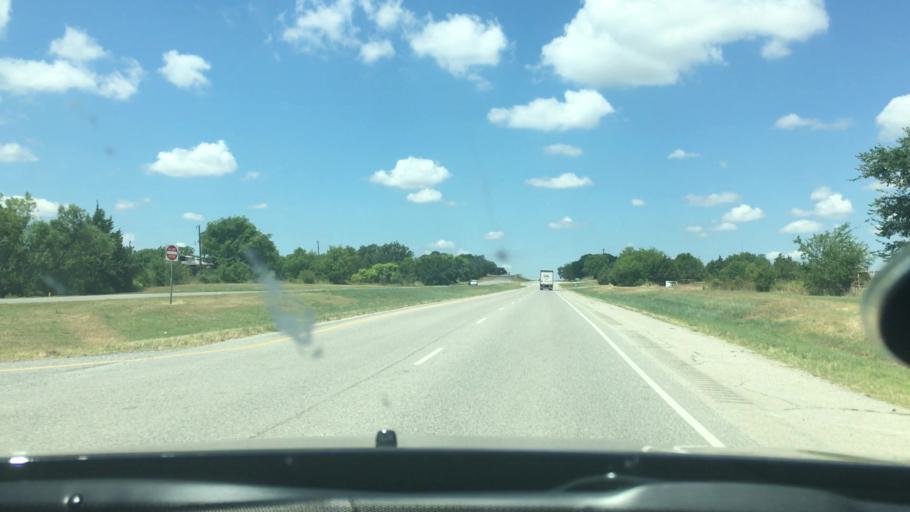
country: US
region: Oklahoma
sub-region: Carter County
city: Wilson
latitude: 34.1730
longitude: -97.4002
